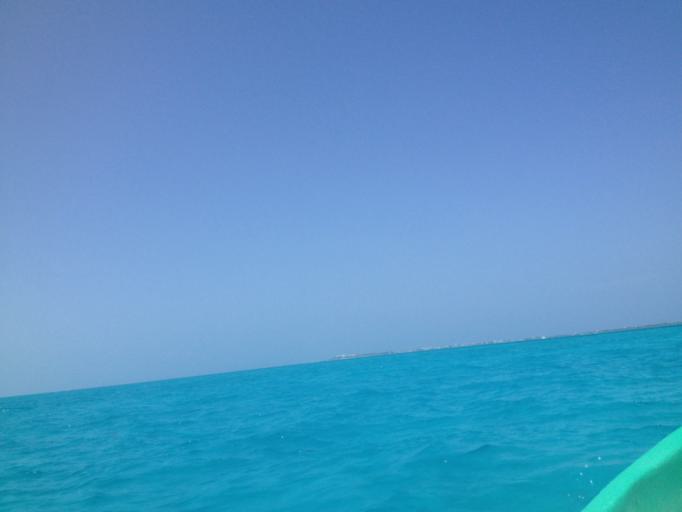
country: MX
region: Quintana Roo
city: Isla Mujeres
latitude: 21.2224
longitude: -86.7717
